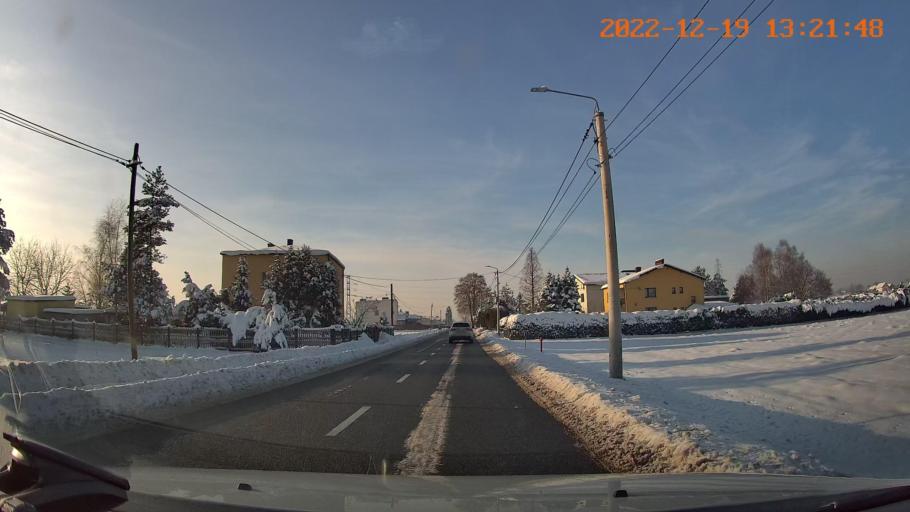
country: PL
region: Silesian Voivodeship
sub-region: Powiat bierunsko-ledzinski
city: Chelm Slaski
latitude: 50.1079
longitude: 19.1785
